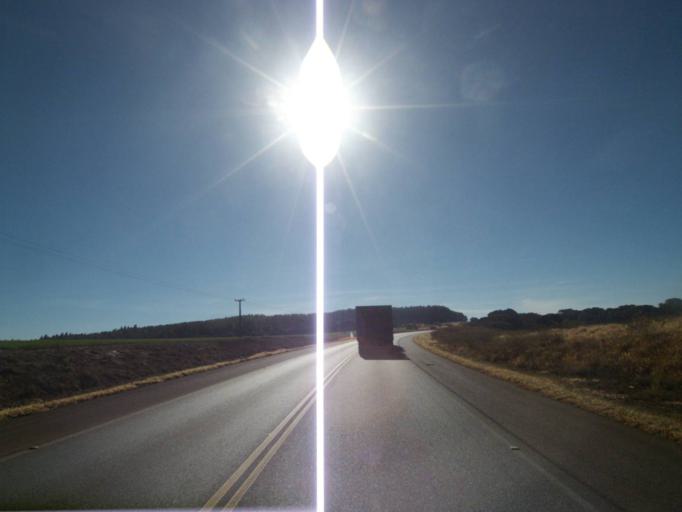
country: BR
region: Parana
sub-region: Tibagi
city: Tibagi
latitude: -24.4380
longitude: -50.4217
